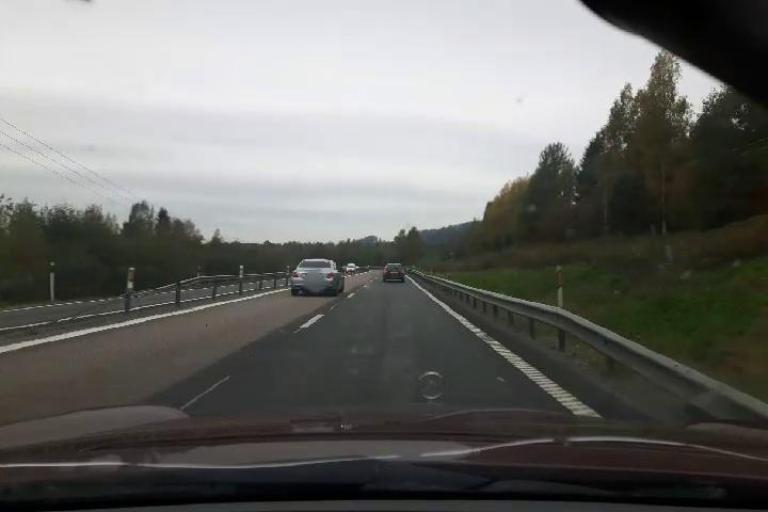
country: SE
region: Vaesternorrland
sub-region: OErnskoeldsviks Kommun
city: Ornskoldsvik
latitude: 63.2976
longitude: 18.6408
